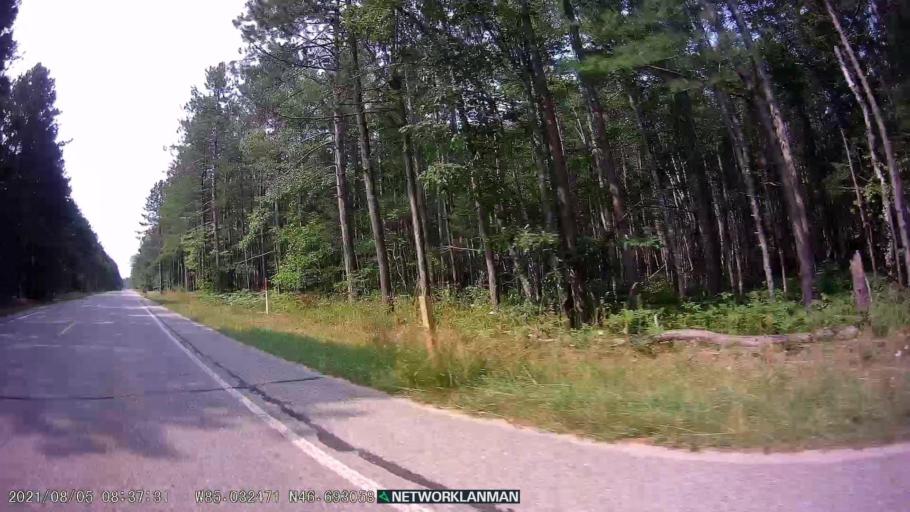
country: US
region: Michigan
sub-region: Luce County
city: Newberry
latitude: 46.6928
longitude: -85.0325
